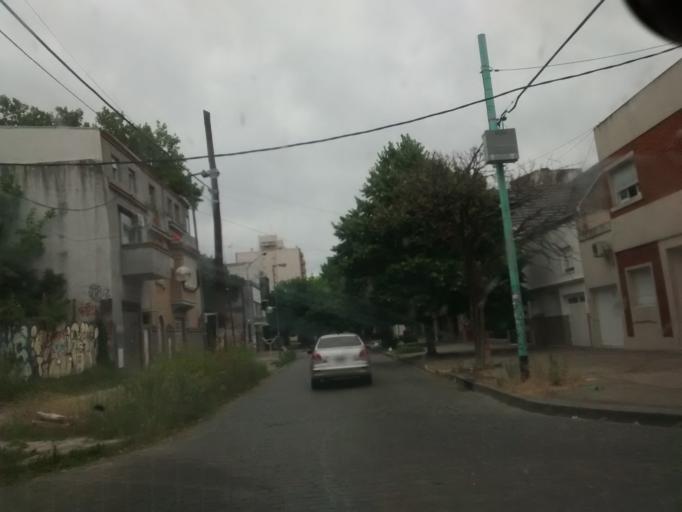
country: AR
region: Buenos Aires
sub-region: Partido de La Plata
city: La Plata
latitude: -34.9245
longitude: -57.9414
